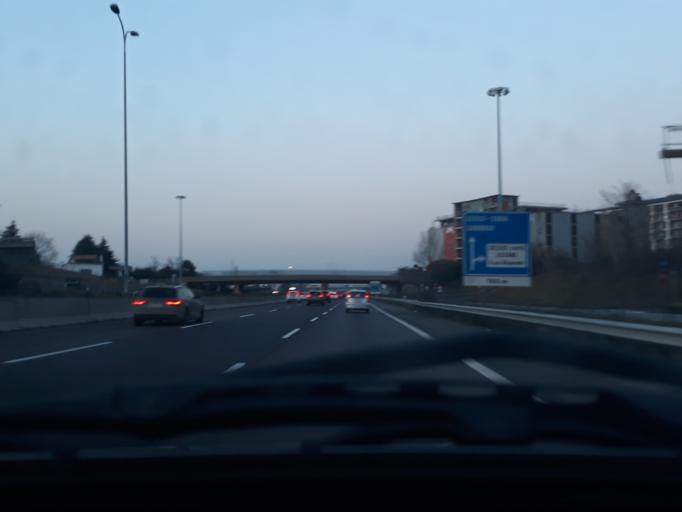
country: IT
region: Lombardy
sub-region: Provincia di Monza e Brianza
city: Santa Margherita
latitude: 45.6191
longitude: 9.2243
